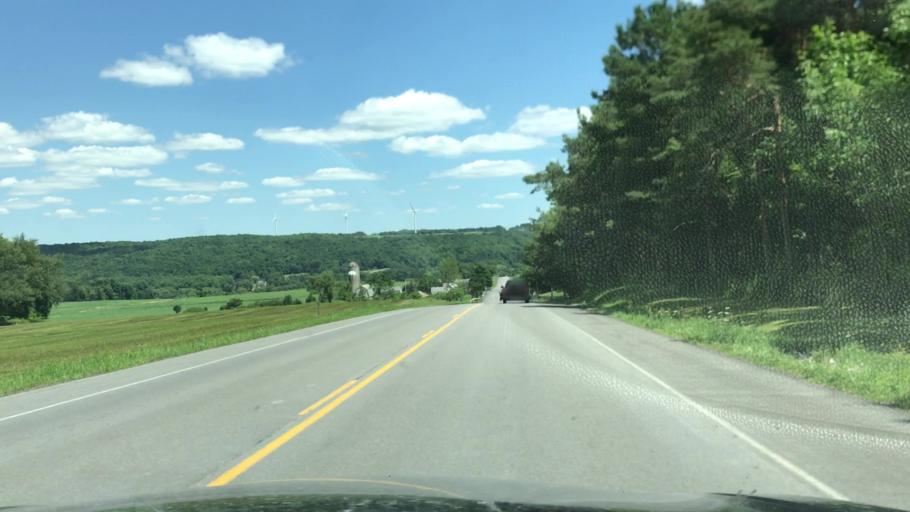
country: US
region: New York
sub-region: Wyoming County
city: Attica
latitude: 42.7703
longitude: -78.3958
